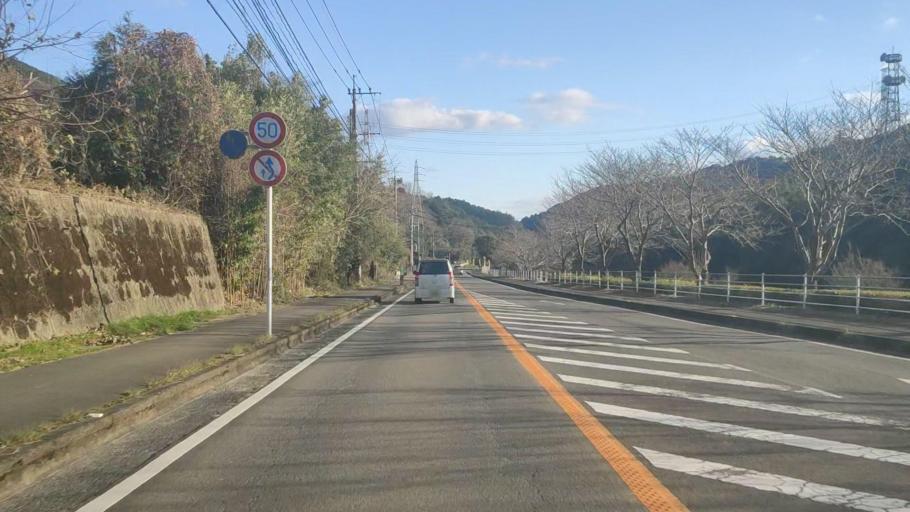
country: JP
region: Saga Prefecture
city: Saga-shi
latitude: 33.3388
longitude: 130.2587
